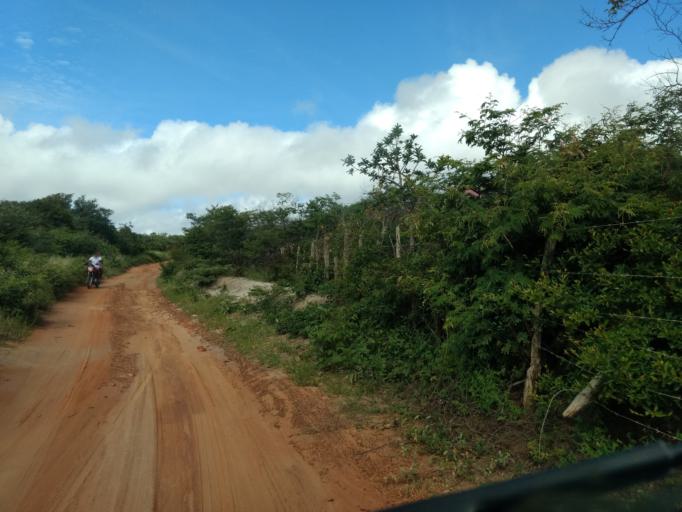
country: BR
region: Ceara
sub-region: Crateus
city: Crateus
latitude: -5.2123
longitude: -40.9435
